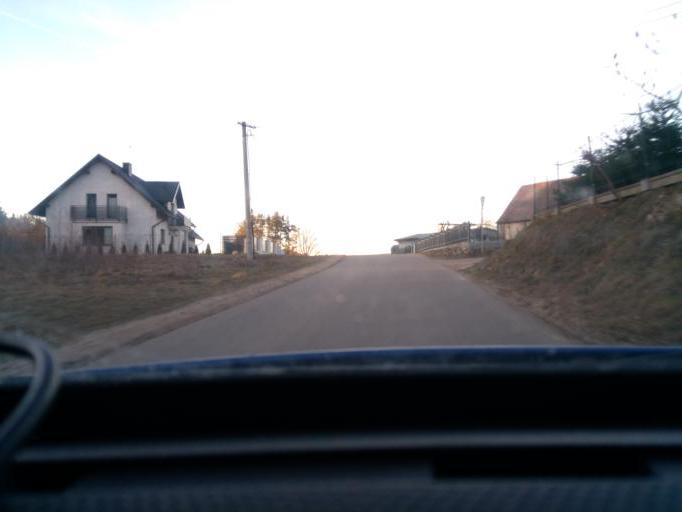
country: PL
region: Pomeranian Voivodeship
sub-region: Powiat kartuski
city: Przodkowo
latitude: 54.3858
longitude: 18.2695
